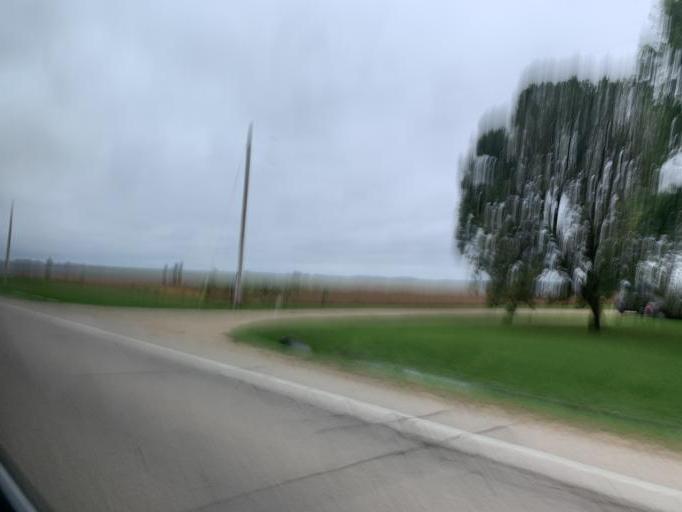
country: US
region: Wisconsin
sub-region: Grant County
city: Muscoda
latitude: 43.2197
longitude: -90.4741
